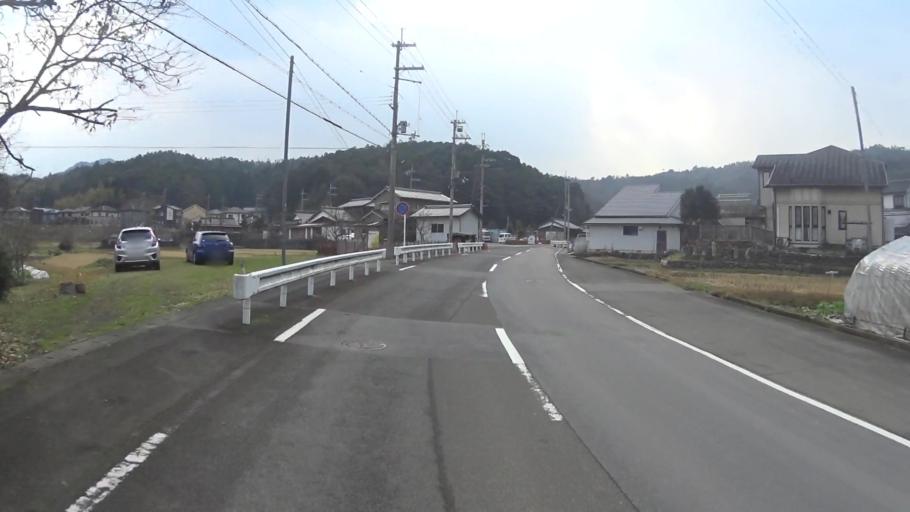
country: JP
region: Kyoto
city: Maizuru
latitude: 35.4426
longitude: 135.2957
